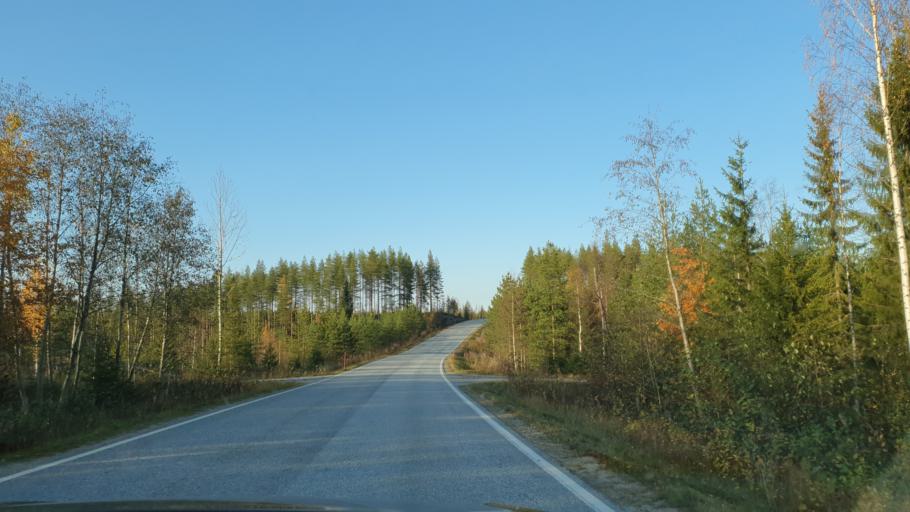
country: FI
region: Kainuu
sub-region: Kehys-Kainuu
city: Kuhmo
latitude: 64.3644
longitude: 29.4888
